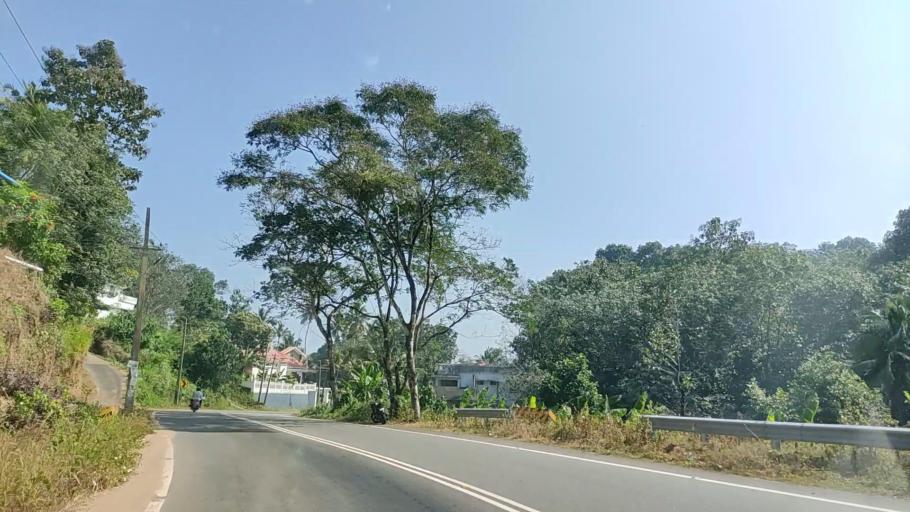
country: IN
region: Kerala
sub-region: Kollam
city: Punalur
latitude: 8.9303
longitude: 76.9947
